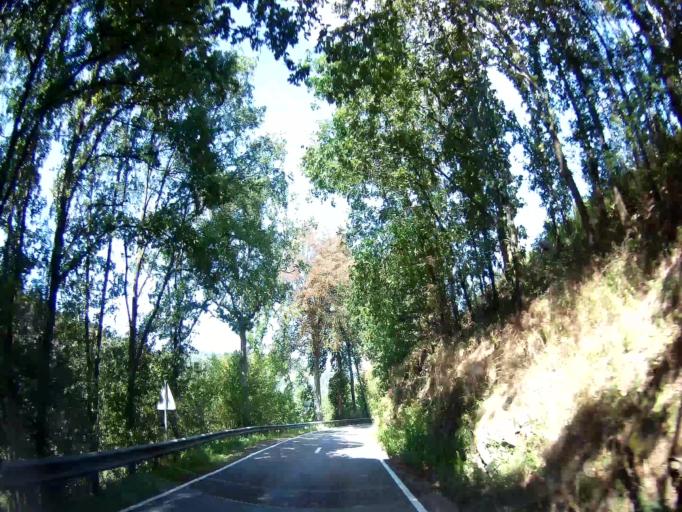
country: BE
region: Wallonia
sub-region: Province du Luxembourg
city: La Roche-en-Ardenne
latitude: 50.1717
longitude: 5.5833
